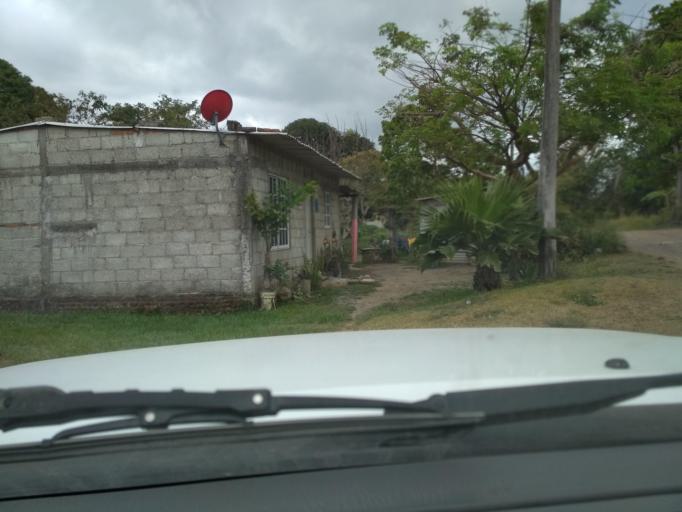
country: MX
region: Veracruz
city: El Tejar
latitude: 19.0617
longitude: -96.1462
